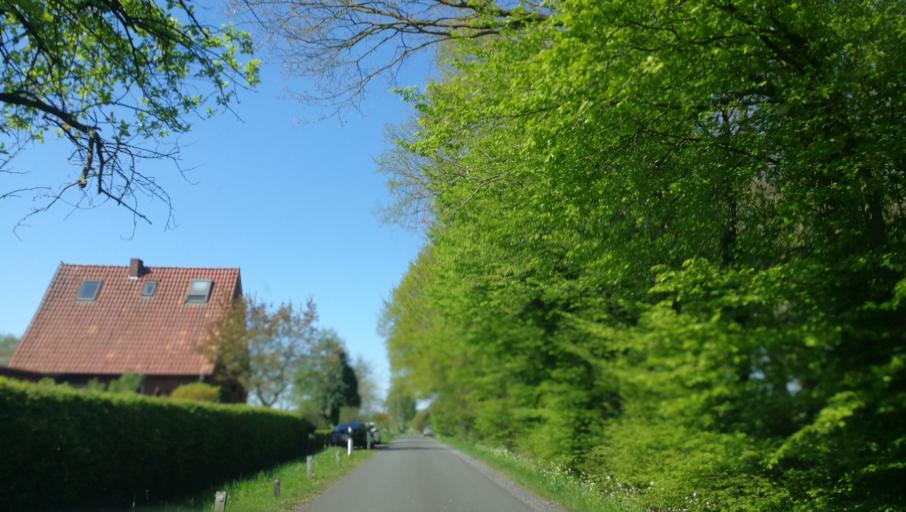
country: DE
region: North Rhine-Westphalia
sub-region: Regierungsbezirk Munster
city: Muenster
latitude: 51.9300
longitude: 7.5602
